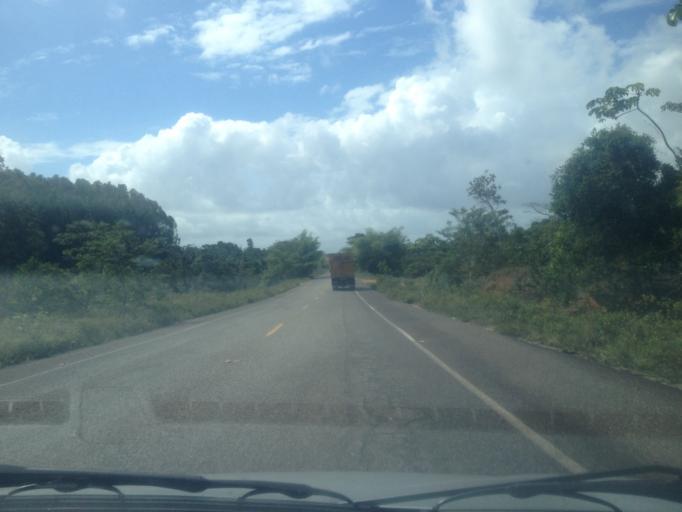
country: BR
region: Sergipe
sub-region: Indiaroba
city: Indiaroba
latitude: -11.6629
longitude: -37.5553
